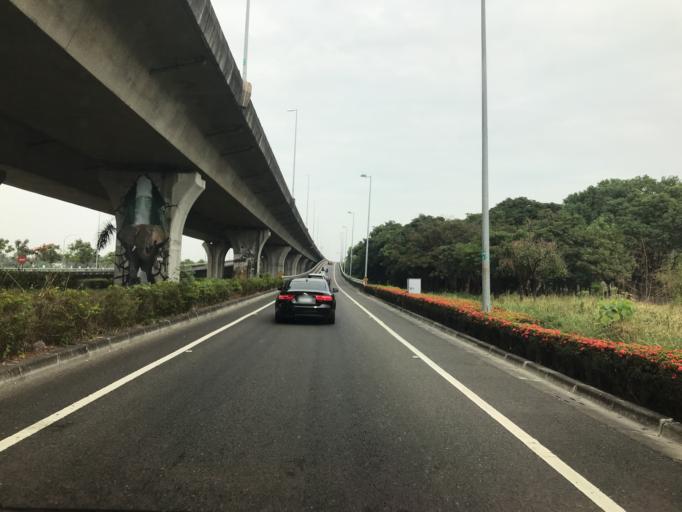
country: TW
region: Taiwan
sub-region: Pingtung
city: Pingtung
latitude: 22.6449
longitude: 120.5416
